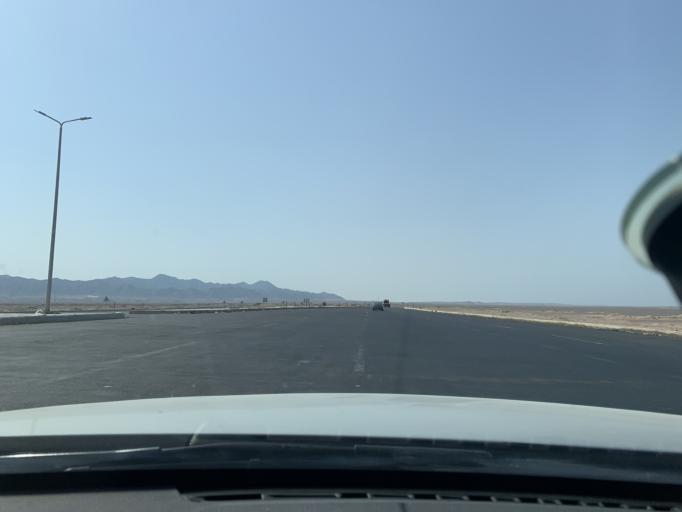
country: EG
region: Red Sea
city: El Gouna
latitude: 27.4323
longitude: 33.6085
